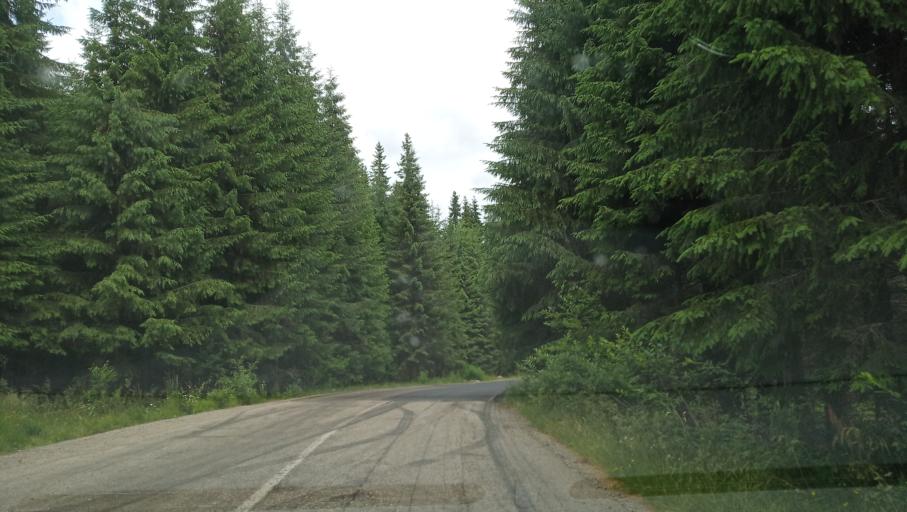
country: RO
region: Gorj
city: Novaci-Straini
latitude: 45.4203
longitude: 23.6975
